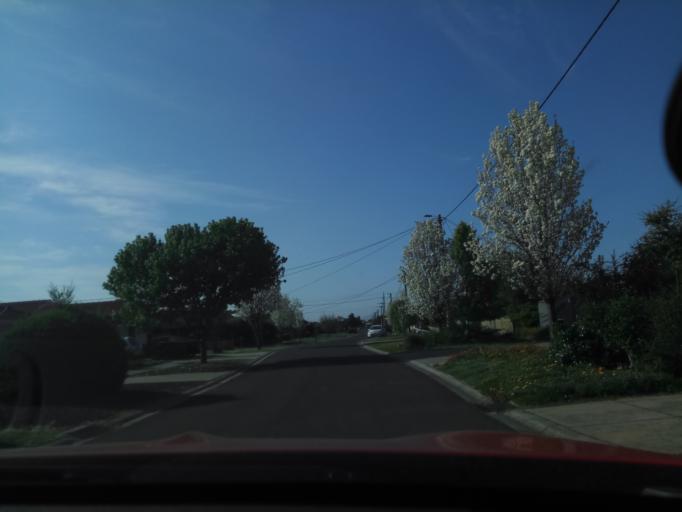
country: AU
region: Victoria
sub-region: Hobsons Bay
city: Laverton
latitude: -37.8777
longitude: 144.7688
